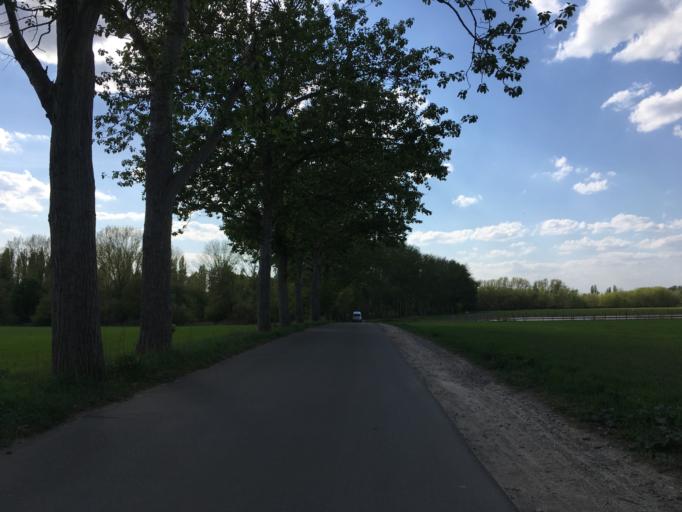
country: DE
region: Berlin
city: Wartenberg
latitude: 52.5771
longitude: 13.5290
